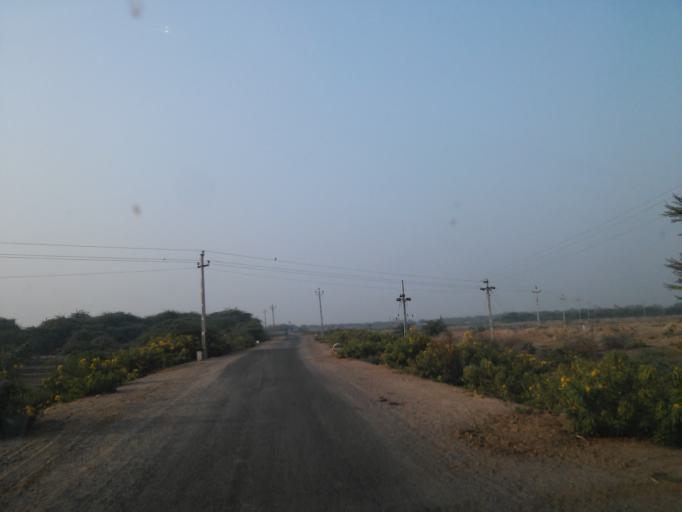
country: IN
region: Gujarat
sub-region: Kachchh
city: Mandvi
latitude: 22.8334
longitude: 69.3893
